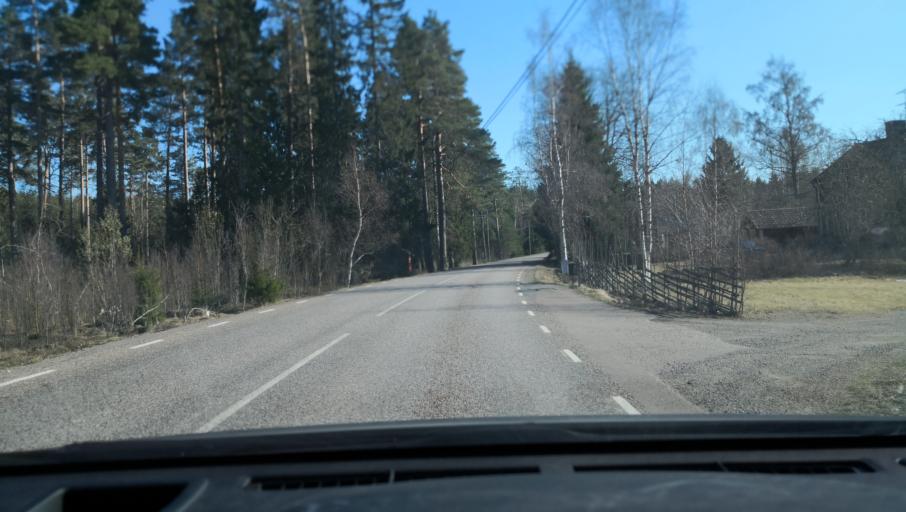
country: SE
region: Dalarna
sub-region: Avesta Kommun
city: Avesta
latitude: 60.0110
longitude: 16.3449
